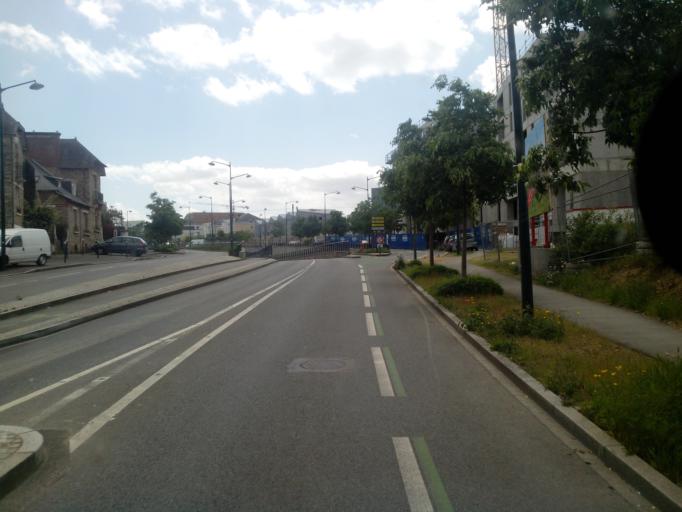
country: FR
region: Brittany
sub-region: Departement d'Ille-et-Vilaine
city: Rennes
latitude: 48.1033
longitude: -1.6940
